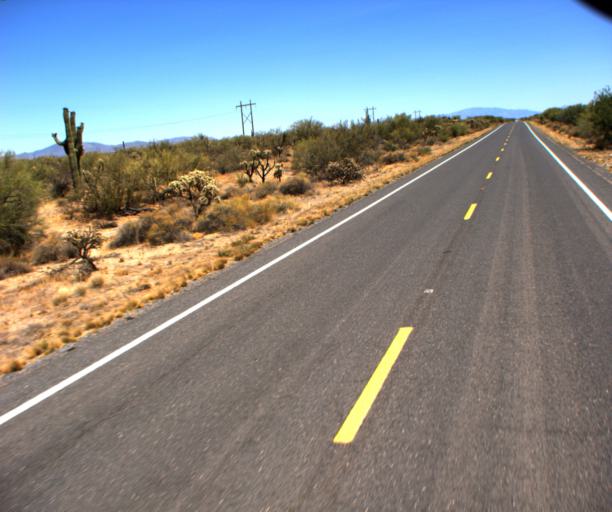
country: US
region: Arizona
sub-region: Pinal County
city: Florence
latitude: 32.8141
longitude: -111.1959
